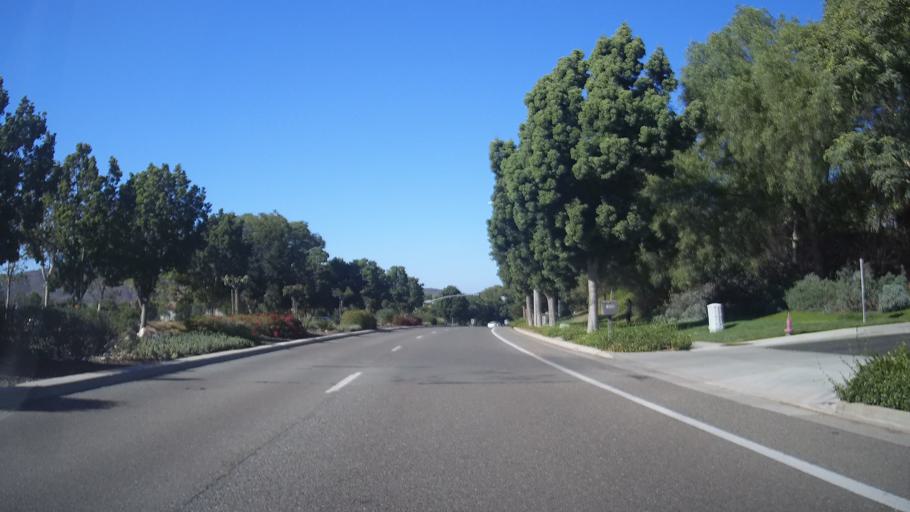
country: US
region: California
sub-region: San Diego County
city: Fairbanks Ranch
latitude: 33.0129
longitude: -117.1121
